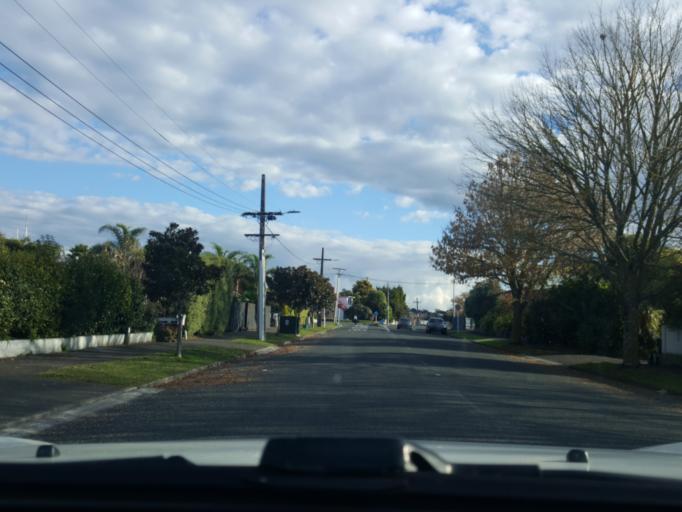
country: NZ
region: Waikato
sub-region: Hamilton City
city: Hamilton
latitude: -37.7715
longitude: 175.2649
